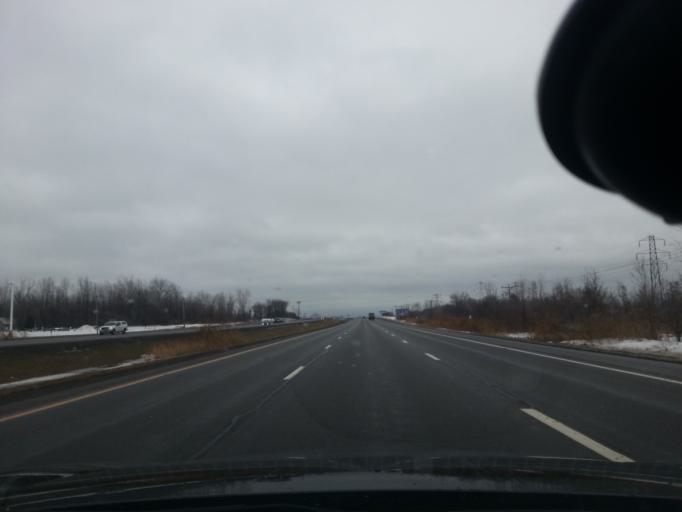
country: US
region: New York
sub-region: Onondaga County
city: North Syracuse
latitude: 43.1870
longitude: -76.1203
